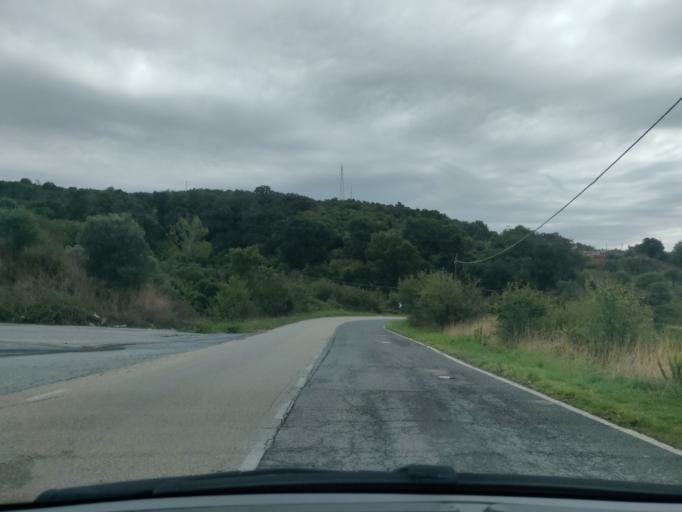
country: IT
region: Latium
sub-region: Citta metropolitana di Roma Capitale
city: Civitavecchia
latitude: 42.1106
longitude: 11.8436
